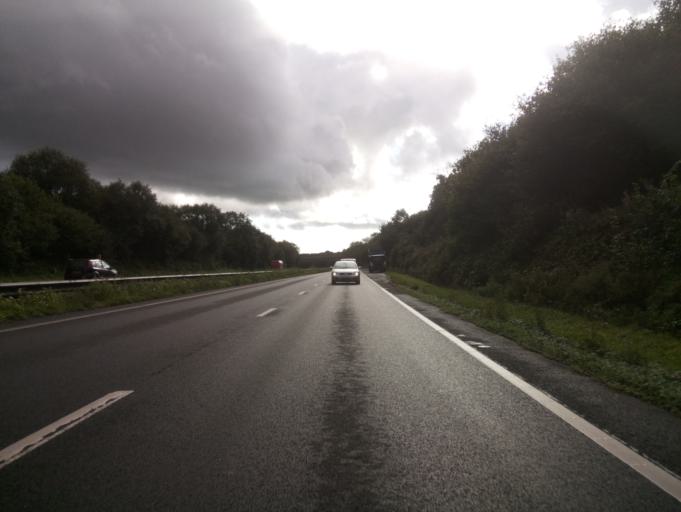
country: GB
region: England
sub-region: Devon
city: South Brent
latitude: 50.4004
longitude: -3.8600
